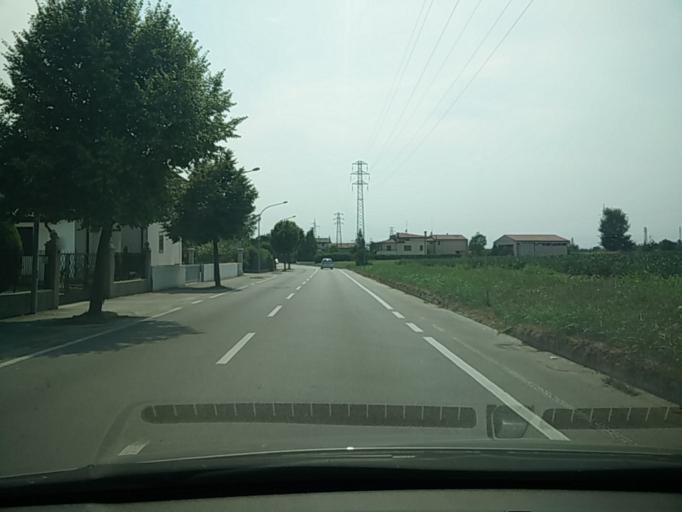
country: IT
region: Veneto
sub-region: Provincia di Treviso
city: San Vendemiano-Fossamerlo
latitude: 45.8795
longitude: 12.3236
